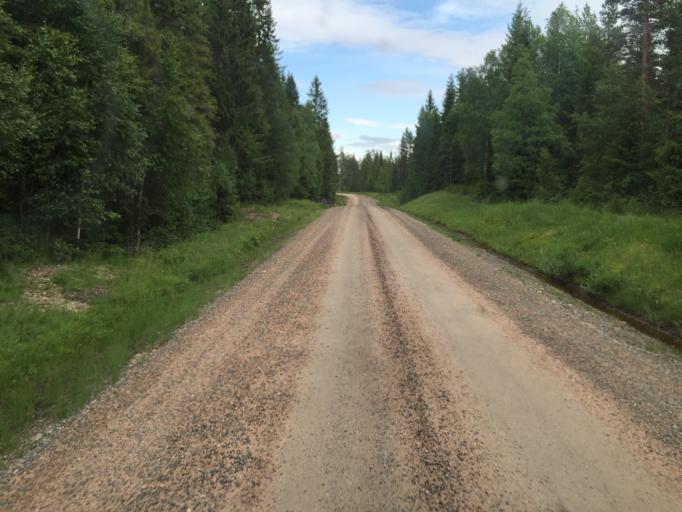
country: SE
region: Dalarna
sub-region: Malung-Saelens kommun
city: Malung
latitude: 60.8927
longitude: 13.6897
